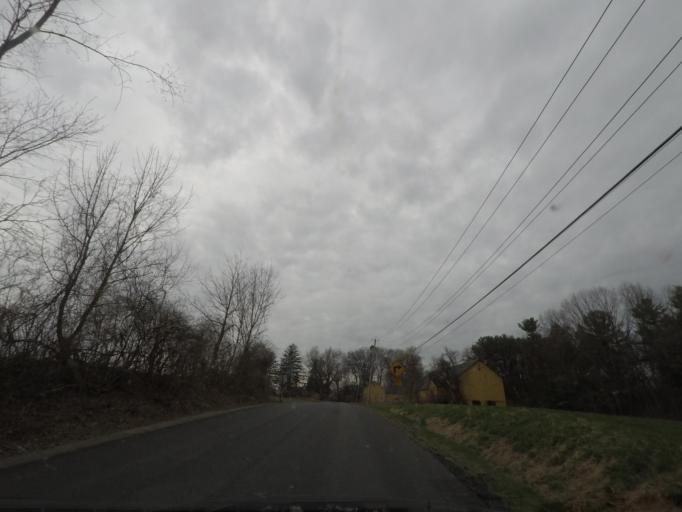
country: US
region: New York
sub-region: Rensselaer County
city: Castleton-on-Hudson
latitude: 42.5555
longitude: -73.7818
